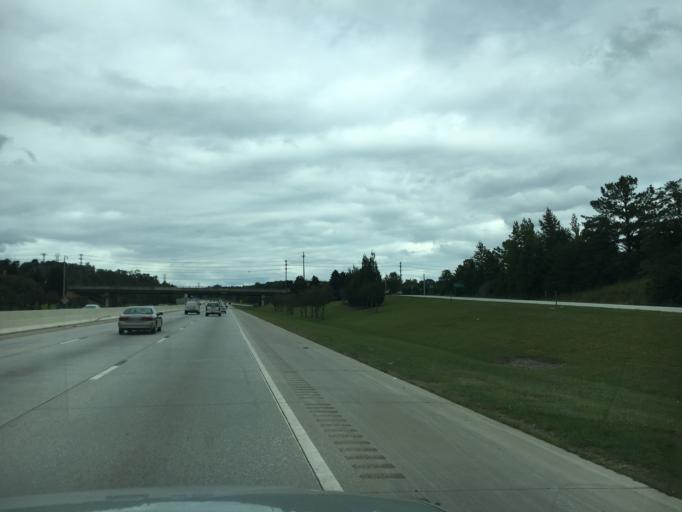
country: US
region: South Carolina
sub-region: Greenville County
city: Mauldin
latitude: 34.7888
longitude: -82.2807
